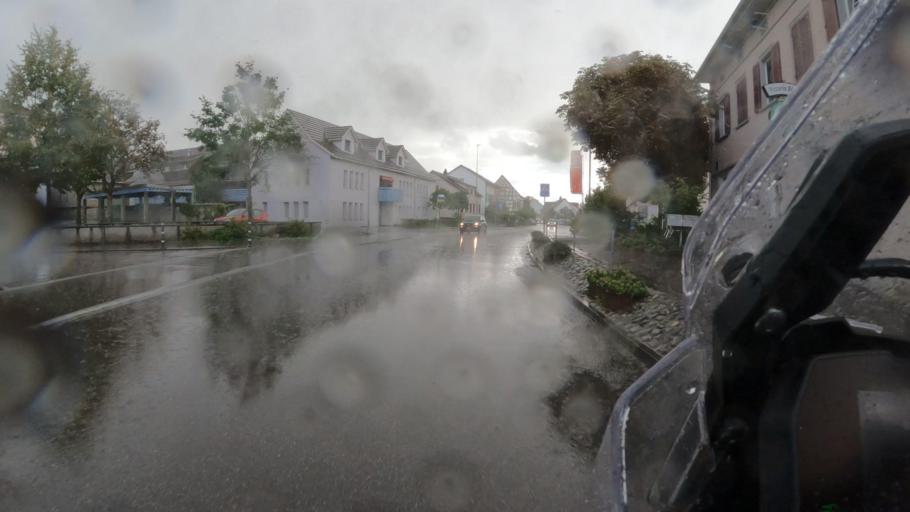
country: CH
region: Zurich
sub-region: Bezirk Andelfingen
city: Dachsen
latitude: 47.6434
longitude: 8.6012
